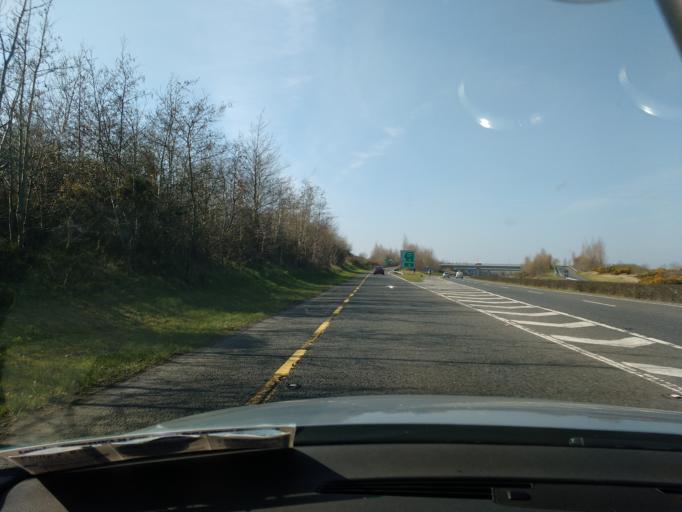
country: IE
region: Munster
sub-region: An Clar
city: Shannon
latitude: 52.7245
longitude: -8.8687
